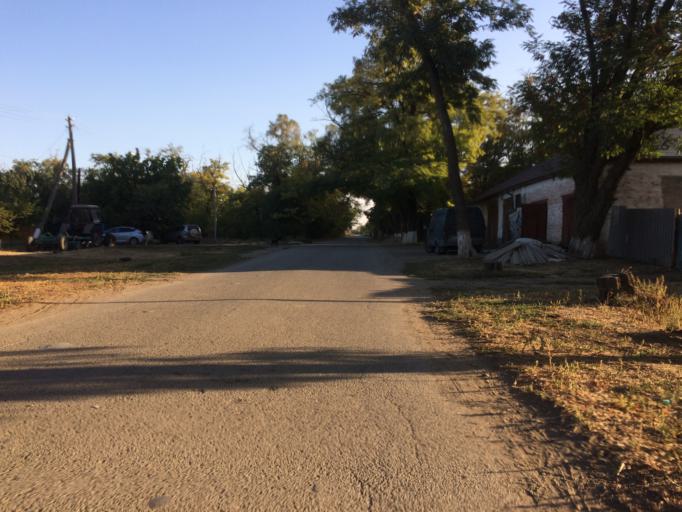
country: RU
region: Rostov
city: Gigant
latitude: 46.5174
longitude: 41.1887
